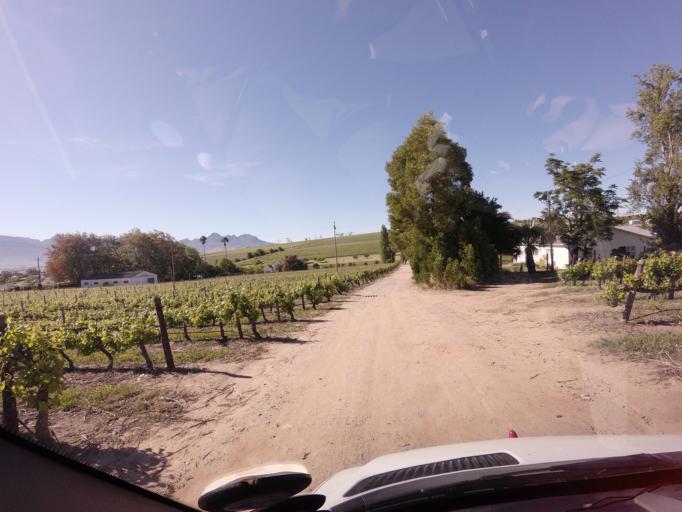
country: ZA
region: Western Cape
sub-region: Cape Winelands District Municipality
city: Stellenbosch
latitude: -33.9505
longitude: 18.7727
